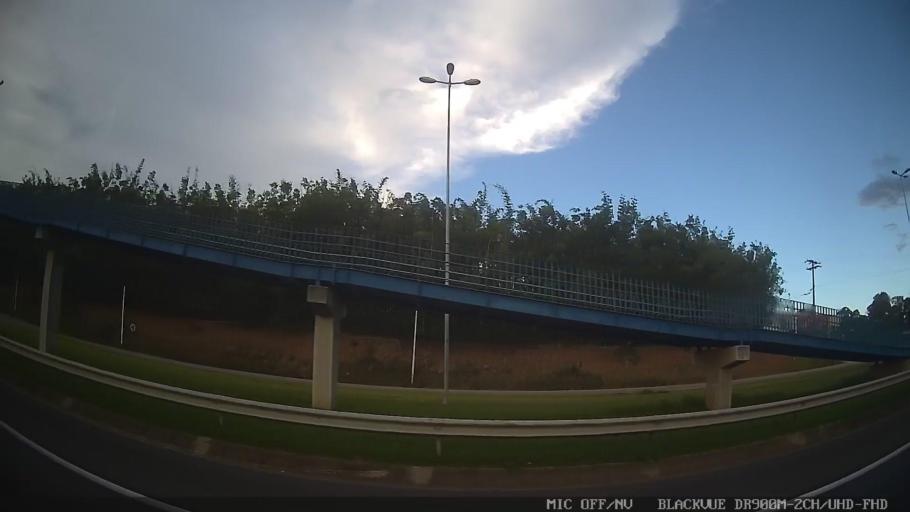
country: BR
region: Sao Paulo
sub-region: Jarinu
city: Jarinu
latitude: -23.0552
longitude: -46.6599
